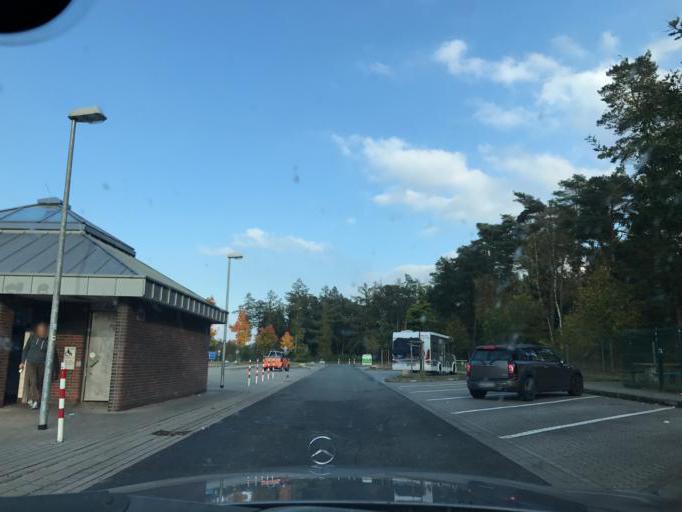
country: DE
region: Lower Saxony
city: Heidenau
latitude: 53.3428
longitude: 9.6562
